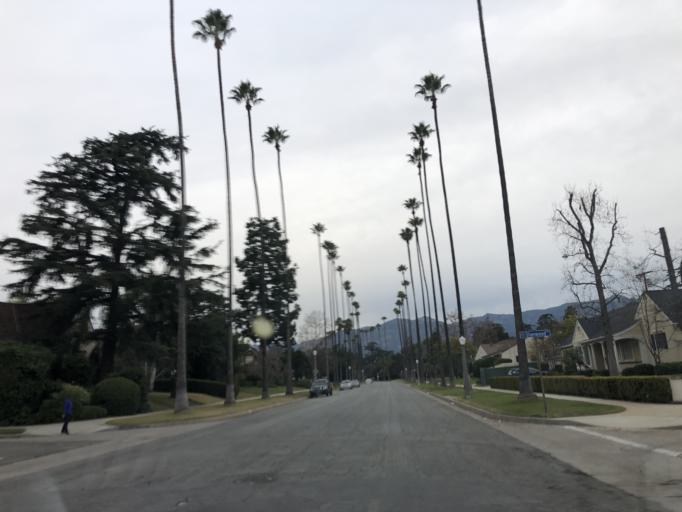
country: US
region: California
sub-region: Los Angeles County
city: San Marino
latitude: 34.1161
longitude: -118.1078
